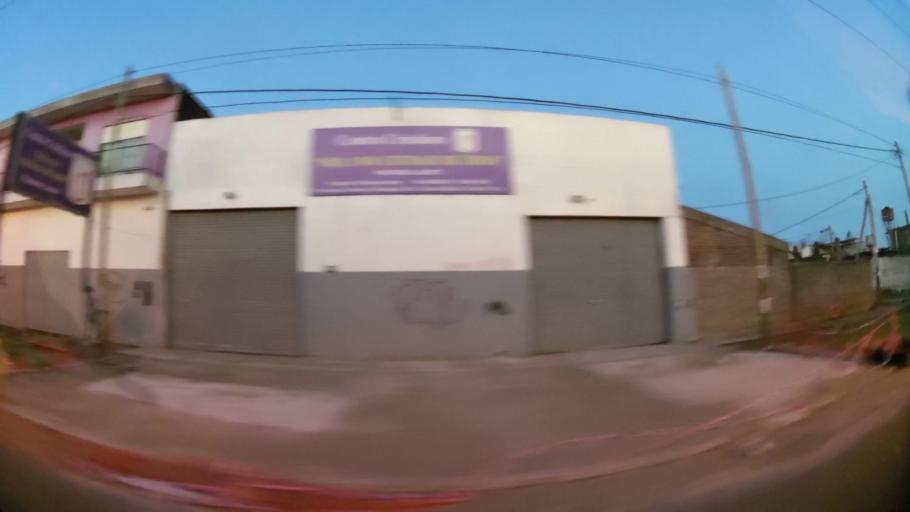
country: AR
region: Buenos Aires
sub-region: Partido de Almirante Brown
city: Adrogue
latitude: -34.7750
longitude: -58.3222
